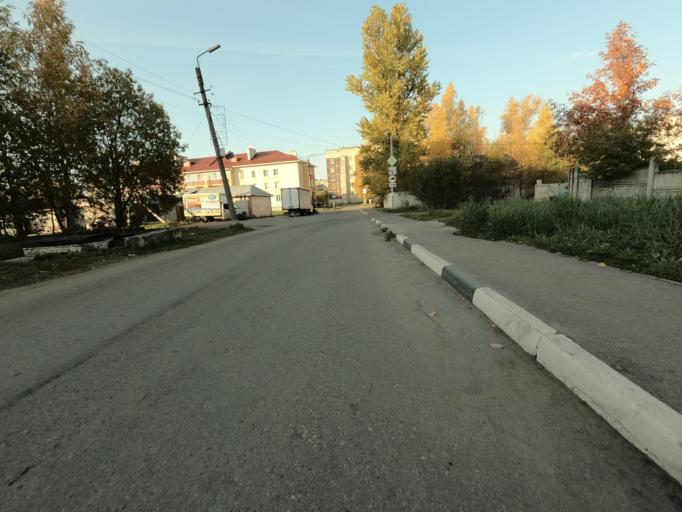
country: RU
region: Leningrad
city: Mga
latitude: 59.7580
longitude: 31.0591
